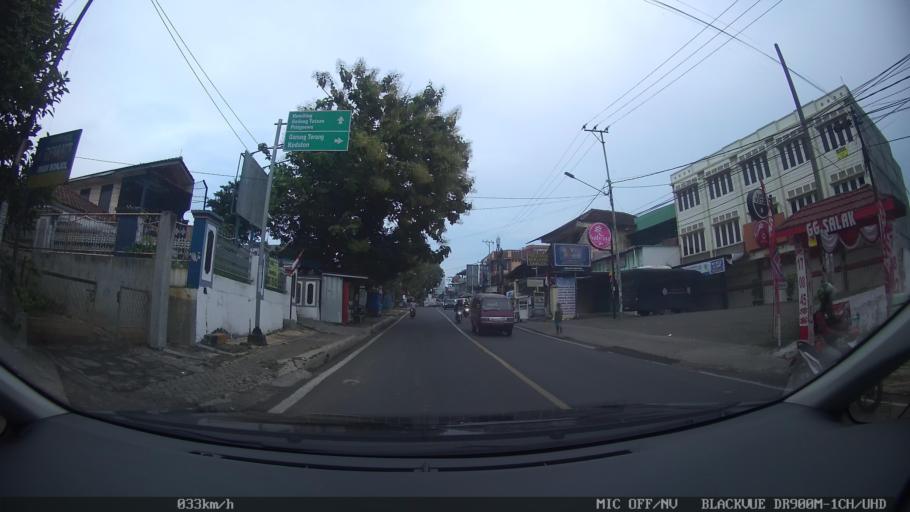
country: ID
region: Lampung
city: Kedaton
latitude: -5.4018
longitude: 105.2486
